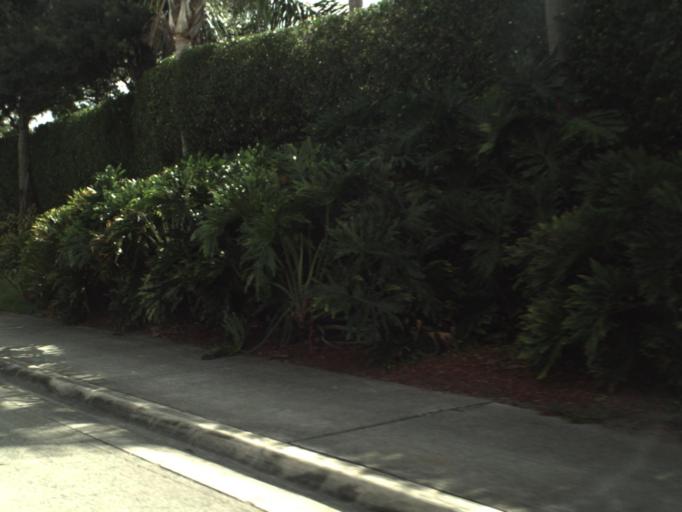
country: US
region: Florida
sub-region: Palm Beach County
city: Villages of Oriole
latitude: 26.5159
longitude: -80.1472
